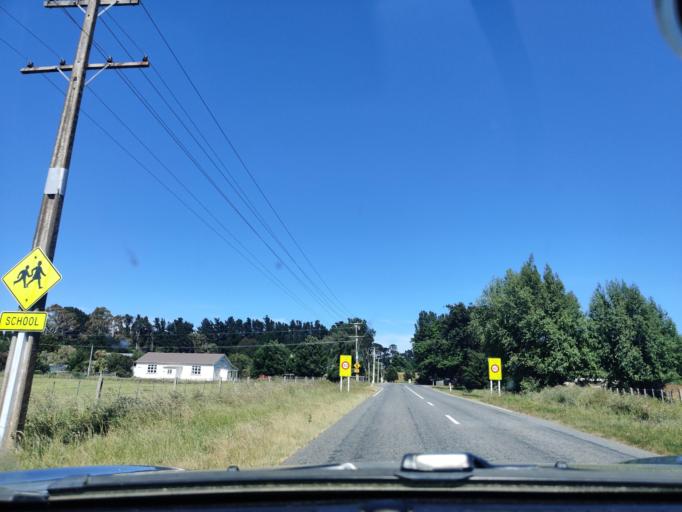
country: NZ
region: Wellington
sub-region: South Wairarapa District
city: Waipawa
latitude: -41.2271
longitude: 175.3432
